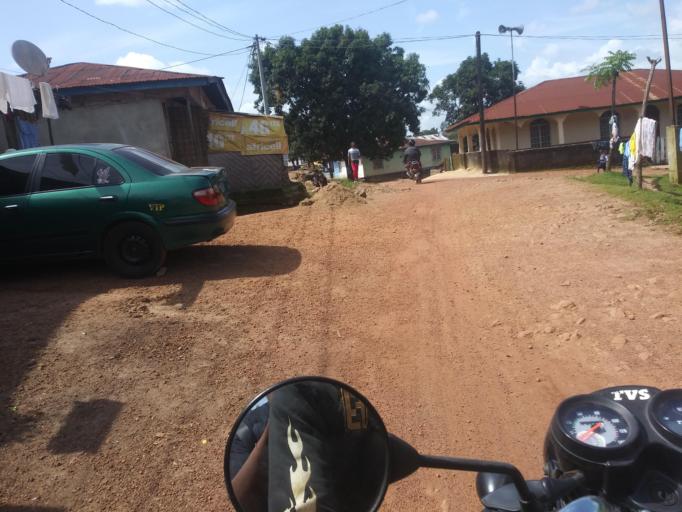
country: SL
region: Northern Province
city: Makeni
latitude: 8.8835
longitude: -12.0352
